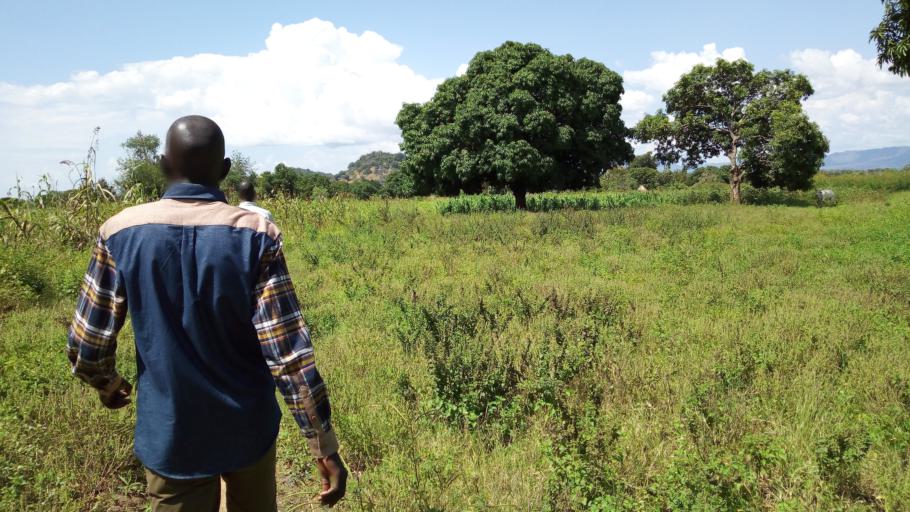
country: UG
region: Northern Region
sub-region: Adjumani District
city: Adjumani
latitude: 3.4599
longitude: 31.8987
